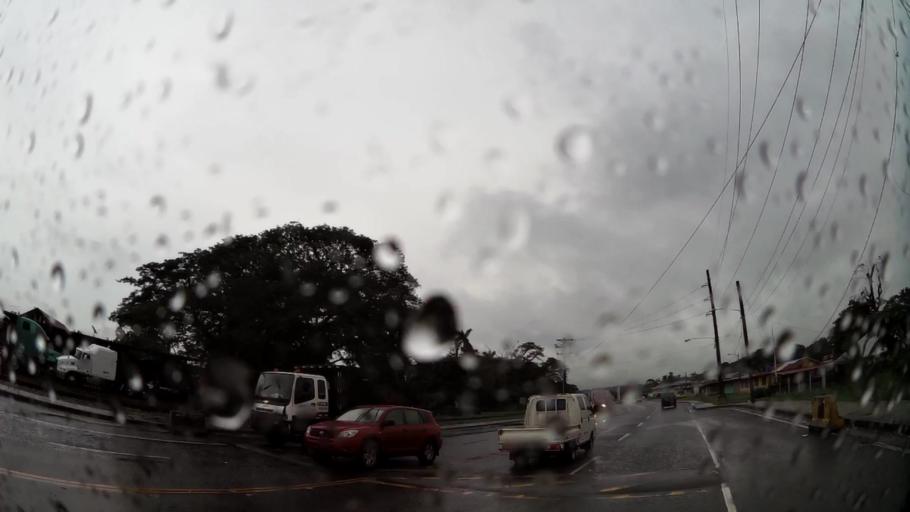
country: PA
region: Colon
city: Arco Iris
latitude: 9.3381
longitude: -79.8918
